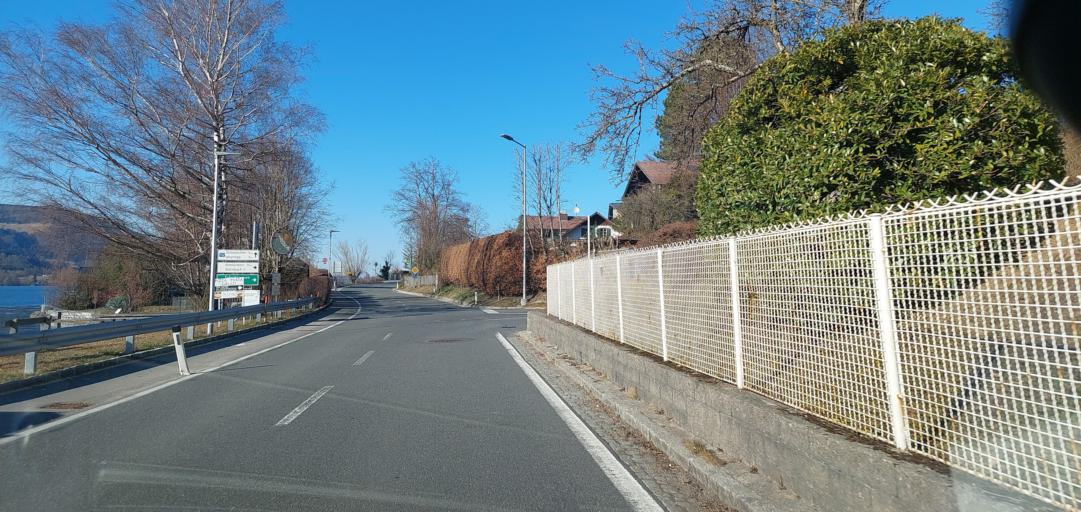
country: AT
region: Upper Austria
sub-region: Politischer Bezirk Vocklabruck
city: Steinbach am Attersee
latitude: 47.8293
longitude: 13.5459
